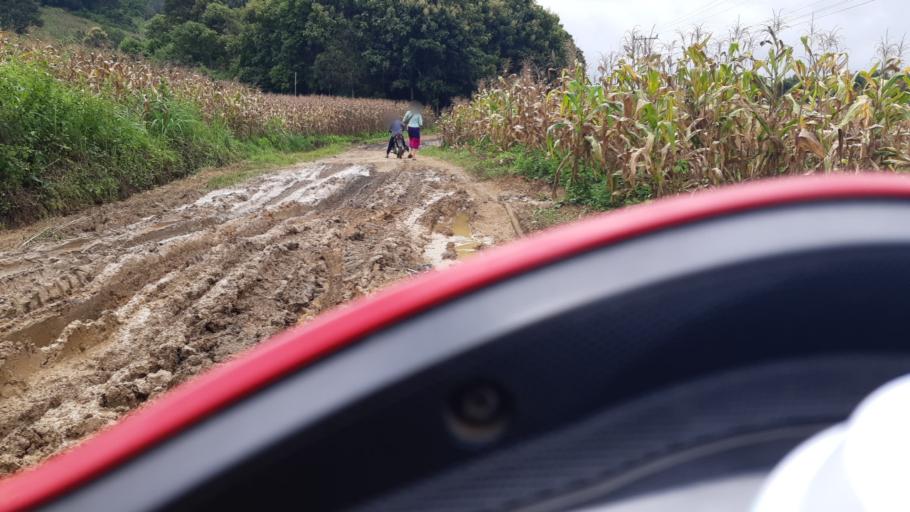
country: LA
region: Loungnamtha
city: Muang Nale
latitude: 20.0183
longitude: 101.5145
